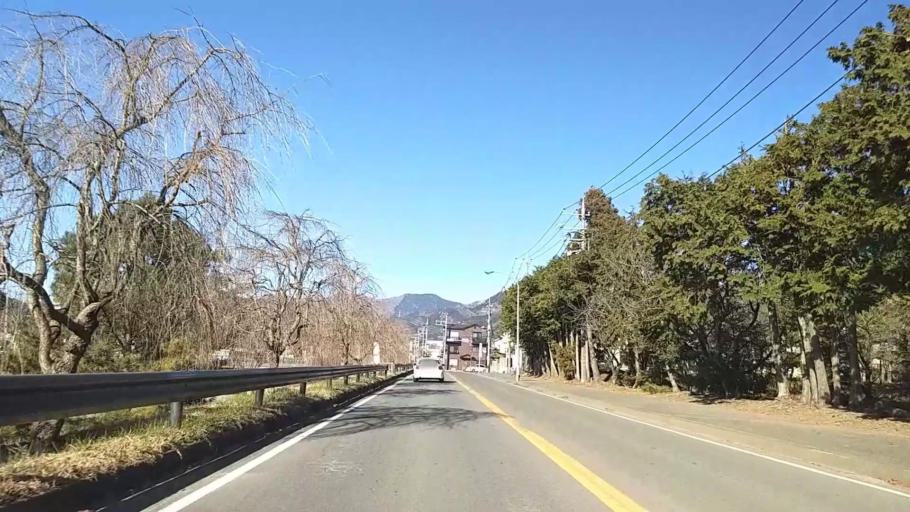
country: JP
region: Kanagawa
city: Hadano
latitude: 35.3925
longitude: 139.1828
